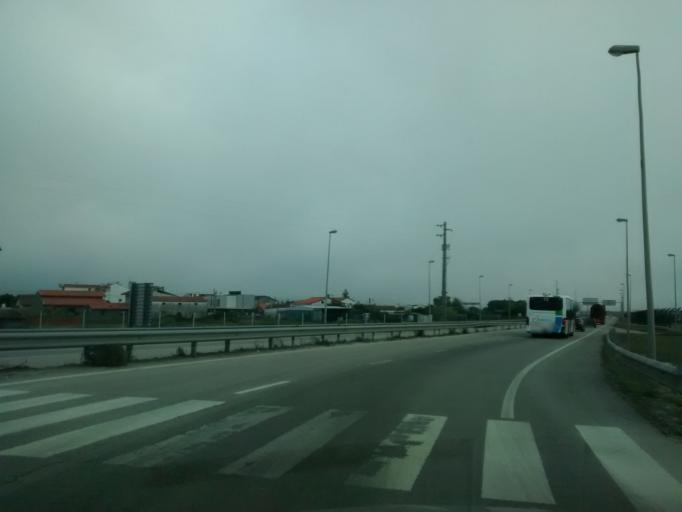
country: PT
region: Aveiro
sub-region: Ilhavo
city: Gafanha da Nazare
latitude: 40.6395
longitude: -8.7263
